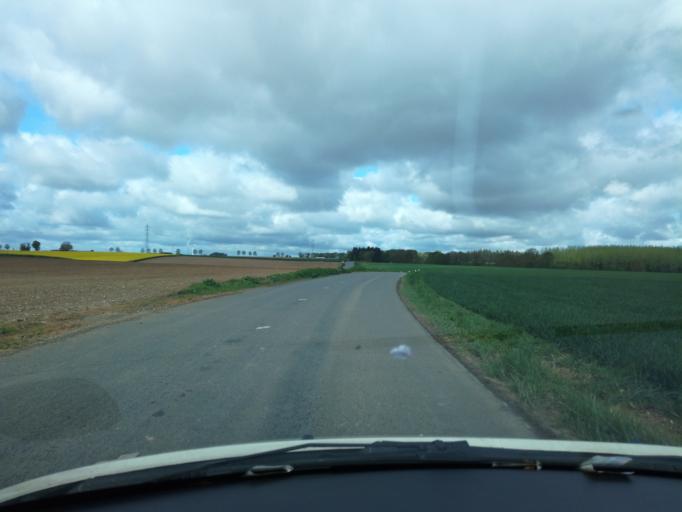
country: FR
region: Picardie
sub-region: Departement de la Somme
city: Poix-de-Picardie
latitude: 49.8159
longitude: 1.9908
